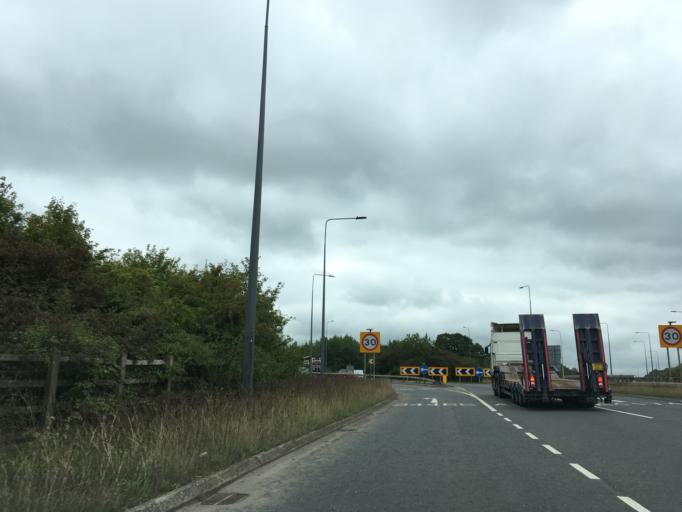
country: GB
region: England
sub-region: South Gloucestershire
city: Siston
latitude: 51.4877
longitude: -2.4695
